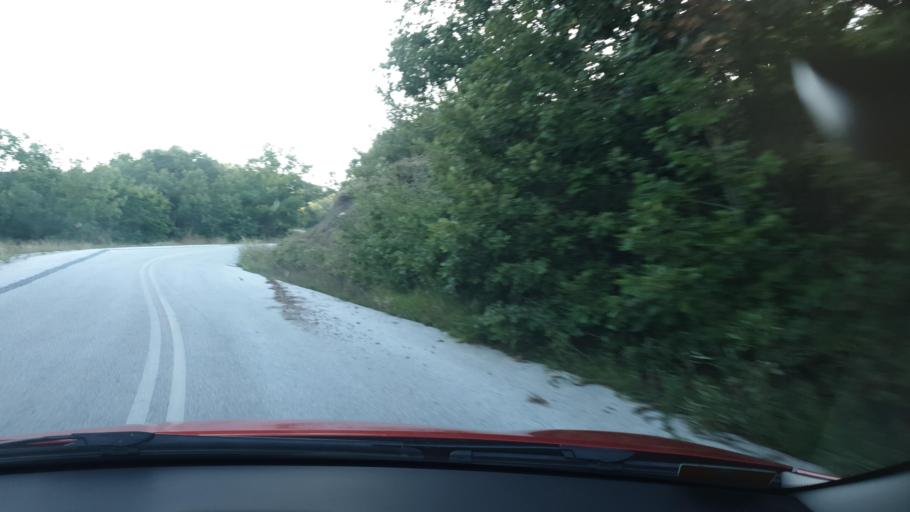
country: GR
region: Central Macedonia
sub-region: Nomos Chalkidikis
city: Galatista
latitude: 40.5113
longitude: 23.2669
